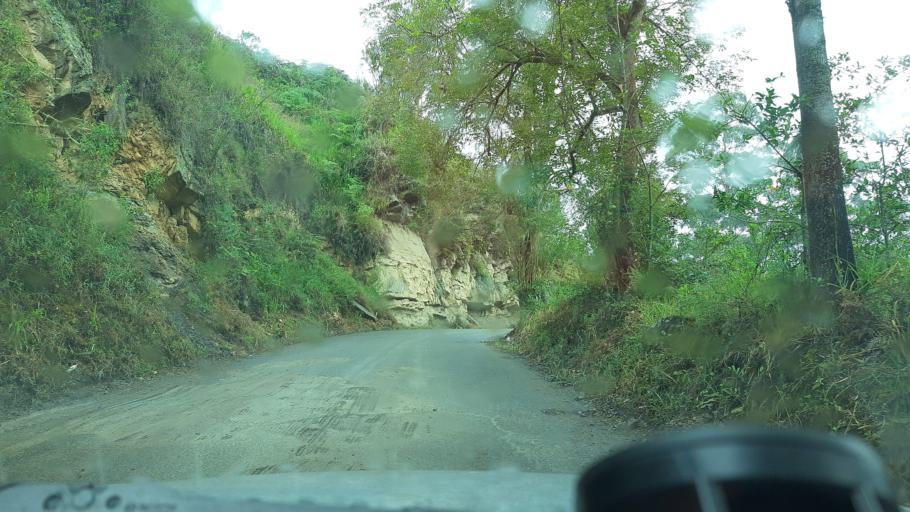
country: CO
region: Boyaca
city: Chinavita
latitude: 5.1693
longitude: -73.3813
